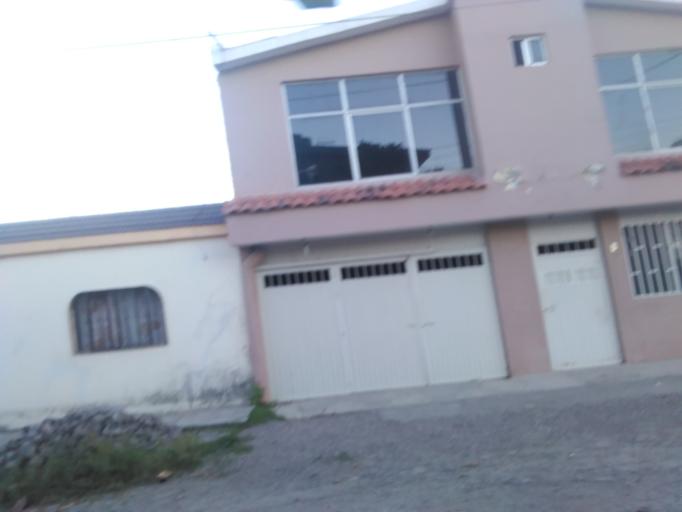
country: MX
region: Nayarit
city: Tepic
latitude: 21.4872
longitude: -104.8932
